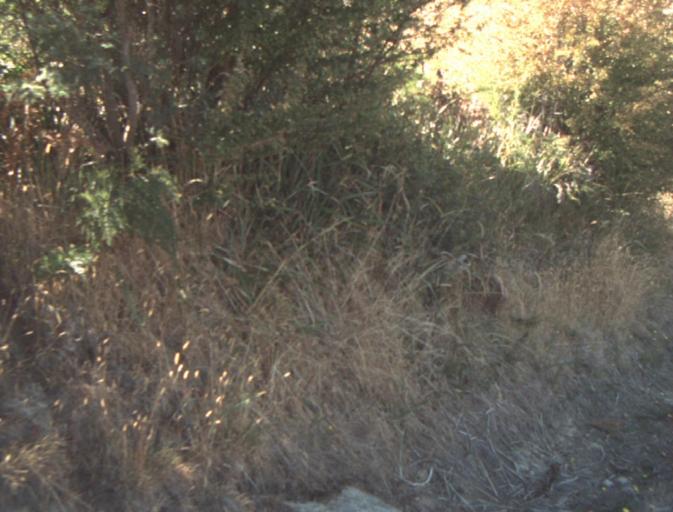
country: AU
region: Tasmania
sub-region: Launceston
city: Newstead
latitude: -41.3517
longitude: 147.3037
